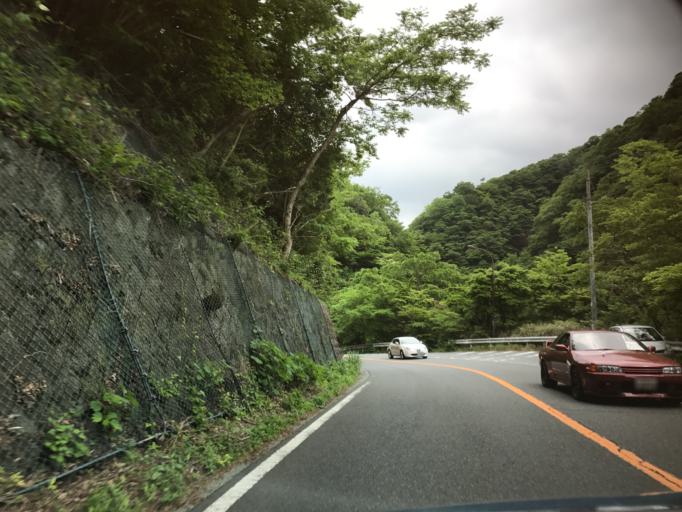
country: JP
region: Kanagawa
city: Hakone
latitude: 35.2636
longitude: 139.0251
